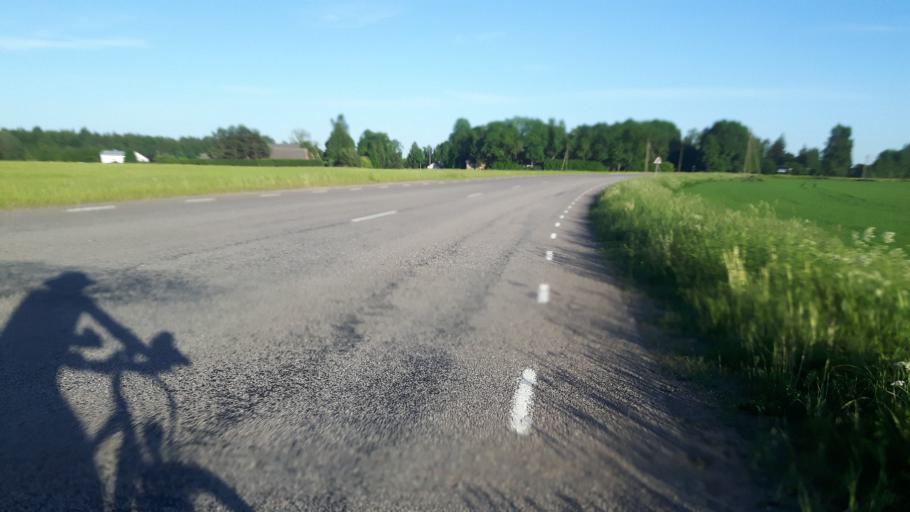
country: EE
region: Raplamaa
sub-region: Jaervakandi vald
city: Jarvakandi
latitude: 58.7998
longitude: 24.9262
